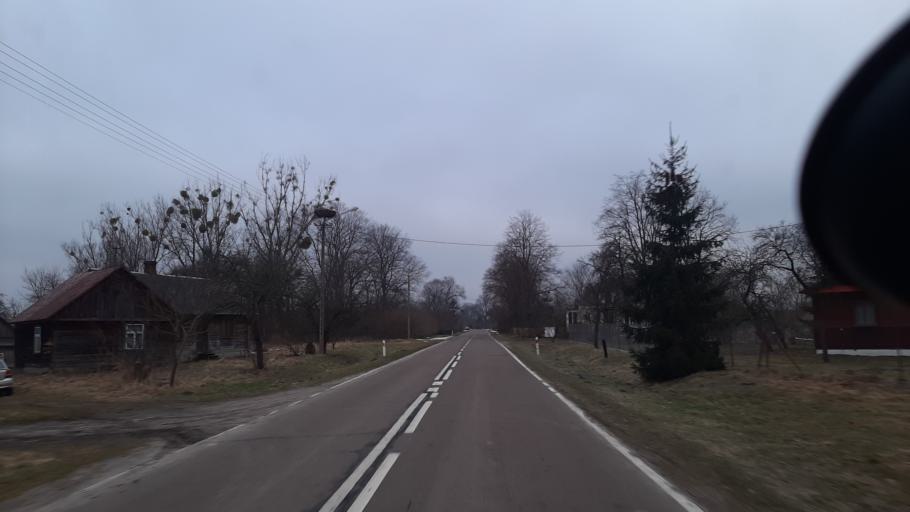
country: PL
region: Lublin Voivodeship
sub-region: Powiat parczewski
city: Podedworze
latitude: 51.5918
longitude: 23.1945
